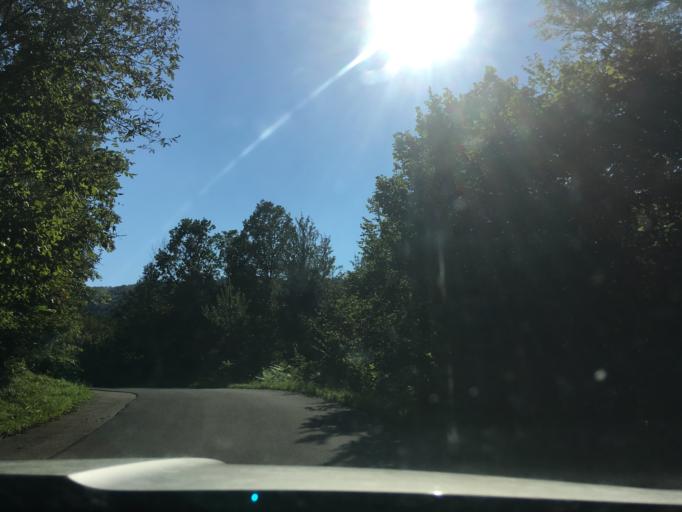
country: HR
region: Primorsko-Goranska
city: Vrbovsko
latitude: 45.4384
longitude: 15.1894
